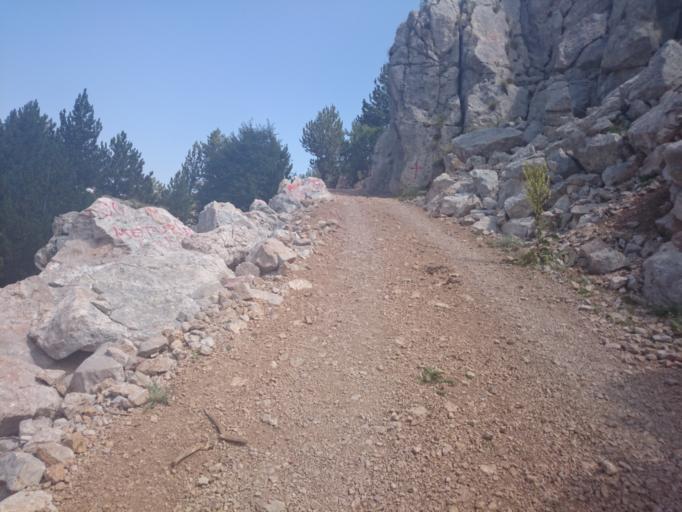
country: AL
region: Lezhe
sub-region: Rrethi i Mirdites
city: Orosh
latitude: 41.8682
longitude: 20.1168
